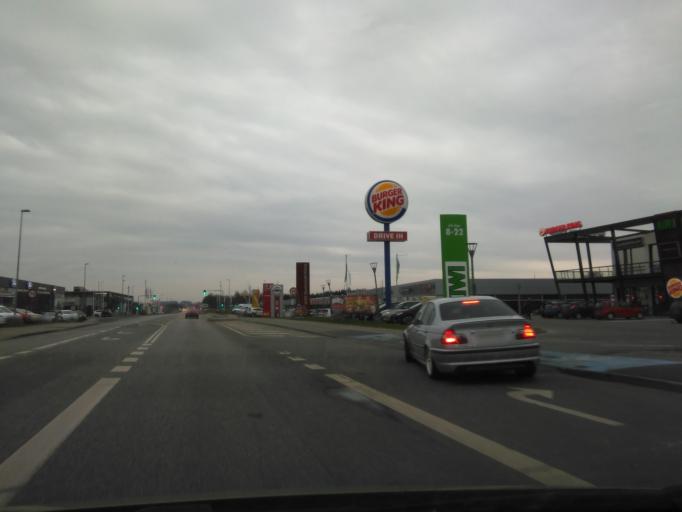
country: DK
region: Central Jutland
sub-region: Randers Kommune
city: Randers
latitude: 56.4391
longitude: 10.0504
